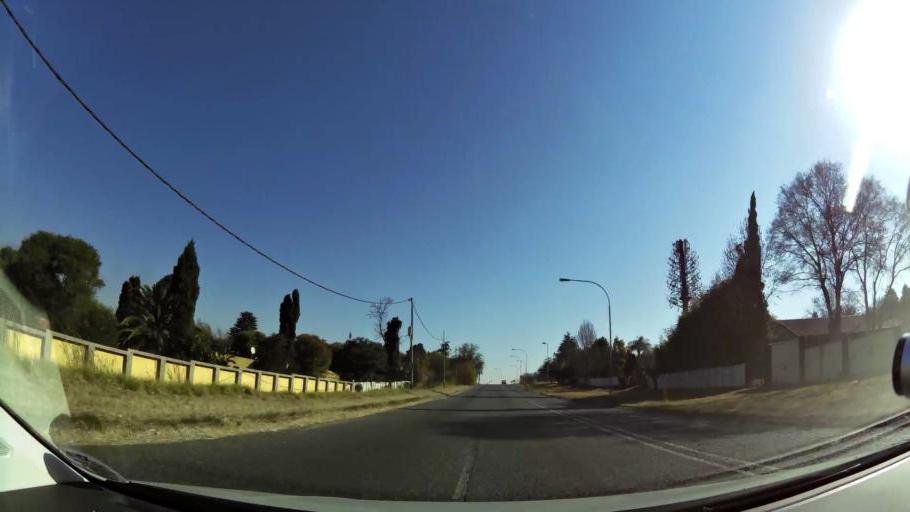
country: ZA
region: Gauteng
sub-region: City of Johannesburg Metropolitan Municipality
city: Modderfontein
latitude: -26.1234
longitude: 28.1220
